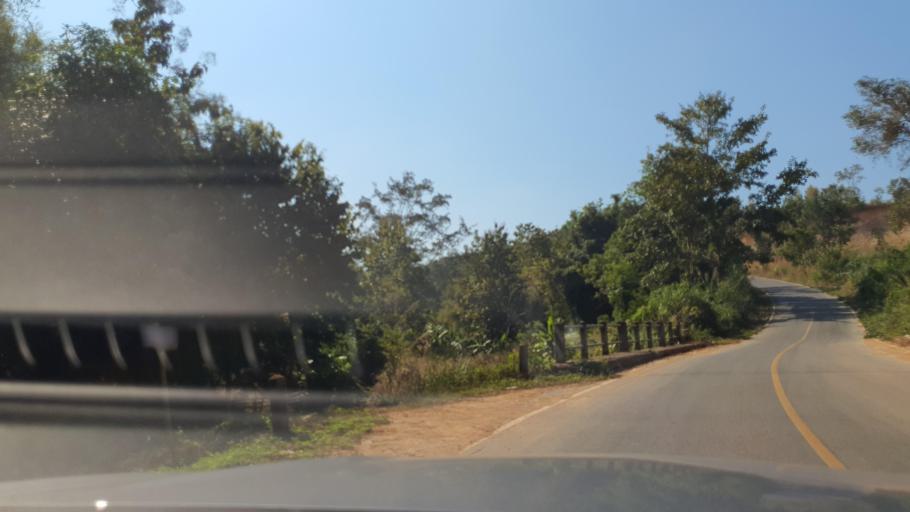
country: TH
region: Nan
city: Pua
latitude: 19.1618
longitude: 100.9076
